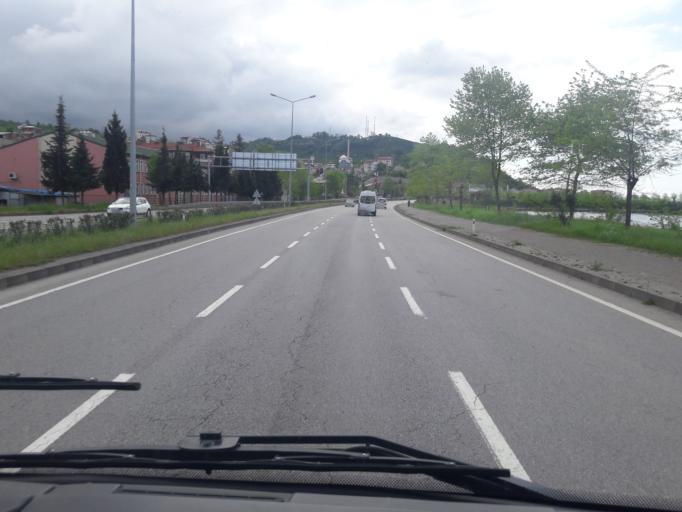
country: TR
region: Giresun
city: Piraziz
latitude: 40.9534
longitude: 38.1276
